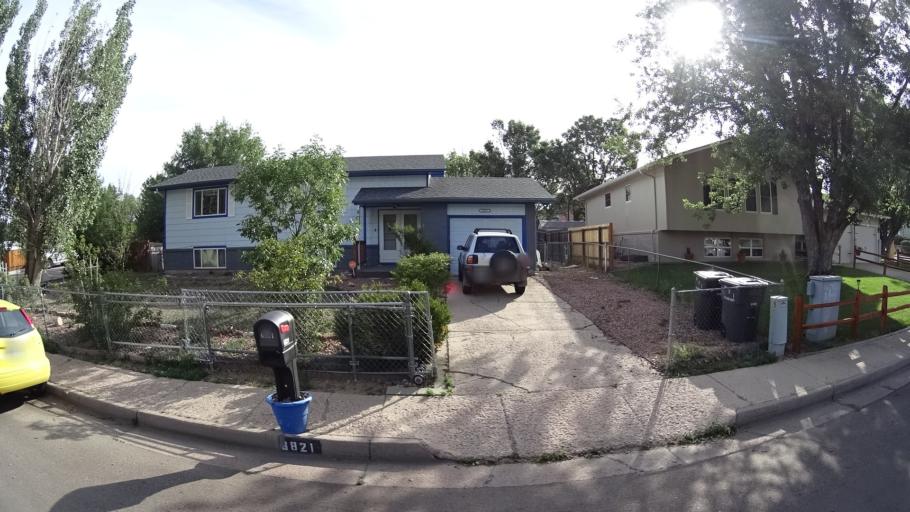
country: US
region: Colorado
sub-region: El Paso County
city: Security-Widefield
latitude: 38.7320
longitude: -104.6934
